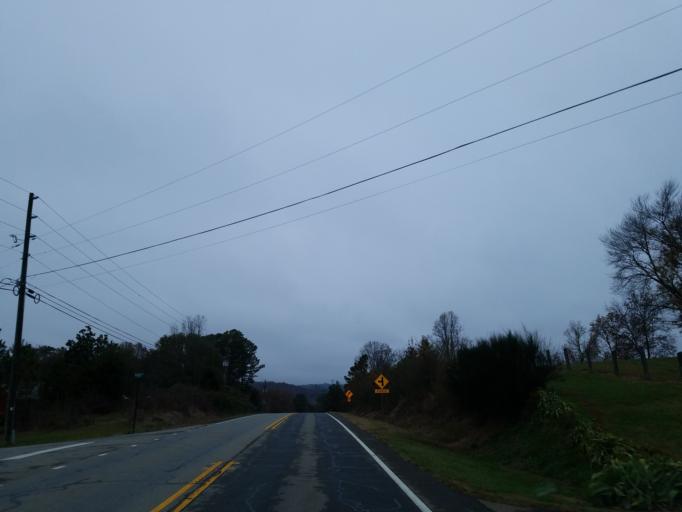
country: US
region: Georgia
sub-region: Pickens County
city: Nelson
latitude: 34.3967
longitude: -84.4329
